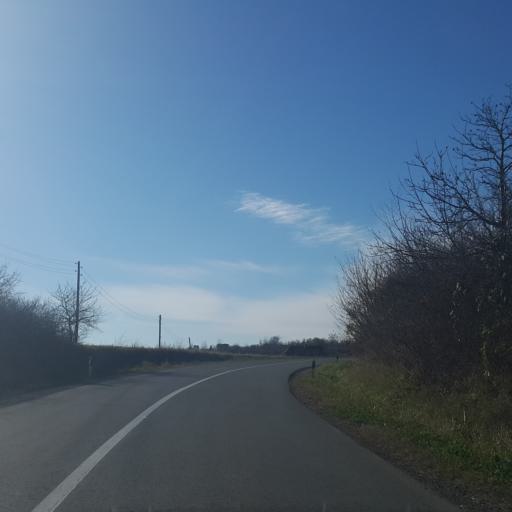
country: RS
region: Central Serbia
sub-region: Sumadijski Okrug
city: Topola
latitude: 44.2517
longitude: 20.7914
